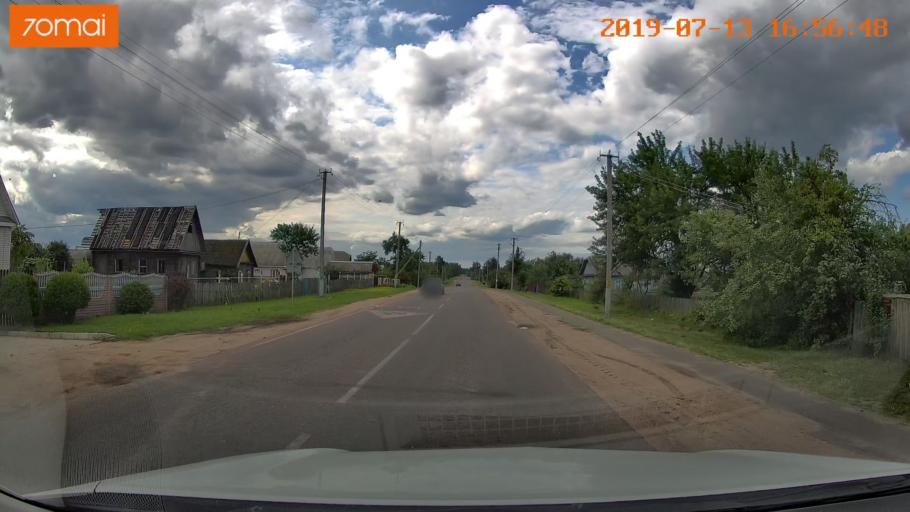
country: BY
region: Mogilev
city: Kirawsk
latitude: 53.2754
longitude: 29.4569
